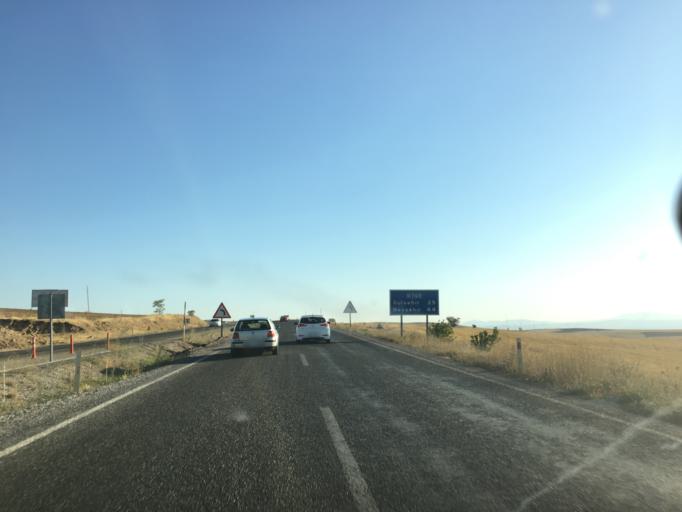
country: TR
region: Nevsehir
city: Hacibektas
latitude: 38.9231
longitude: 34.5456
